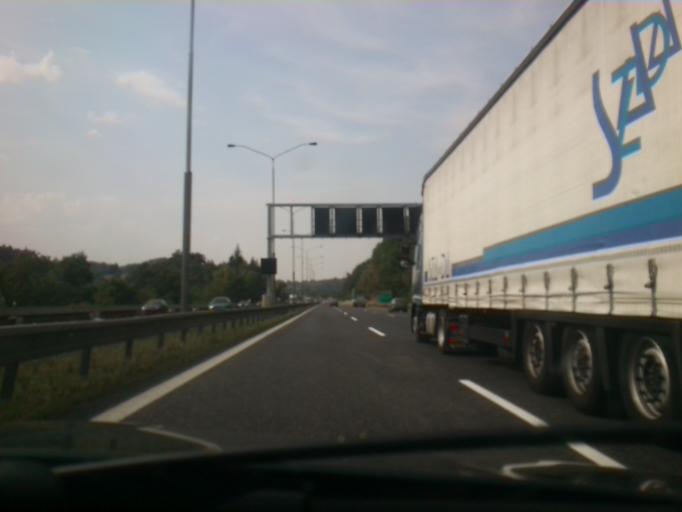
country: CZ
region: Central Bohemia
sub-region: Okres Praha-Vychod
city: Mnichovice
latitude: 49.9185
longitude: 14.7071
